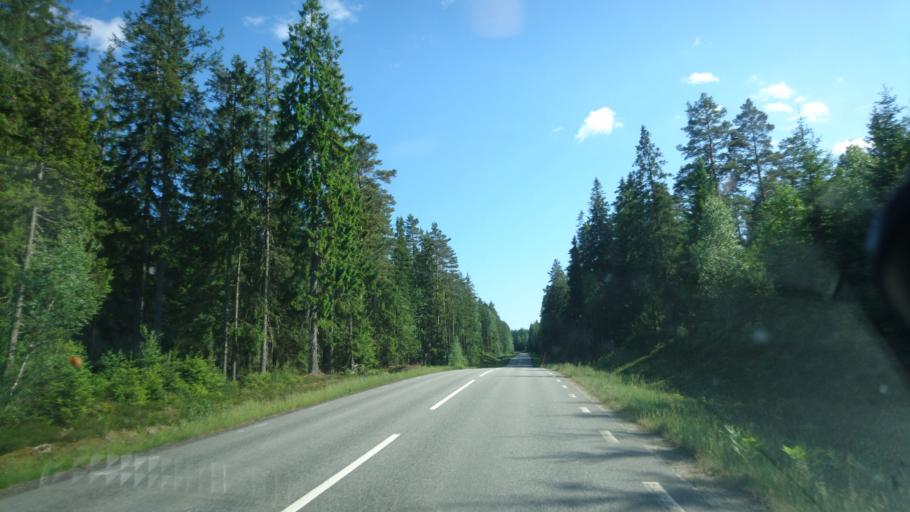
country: SE
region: Skane
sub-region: Osby Kommun
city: Lonsboda
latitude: 56.4602
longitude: 14.2335
